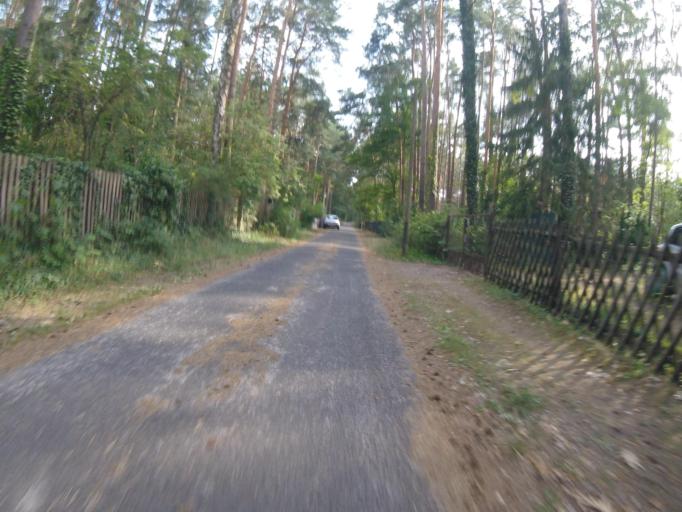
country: DE
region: Brandenburg
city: Munchehofe
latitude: 52.2489
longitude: 13.7792
